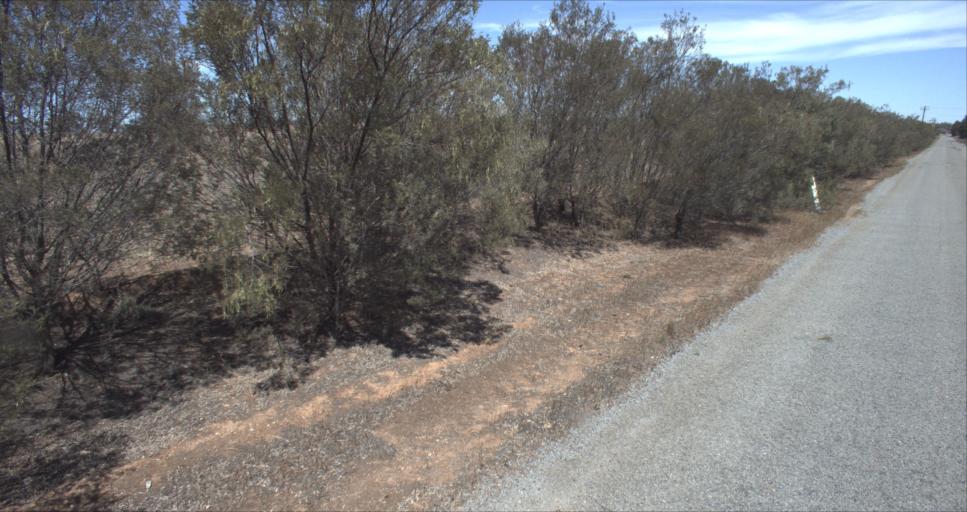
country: AU
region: New South Wales
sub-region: Leeton
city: Leeton
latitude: -34.5897
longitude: 146.4411
